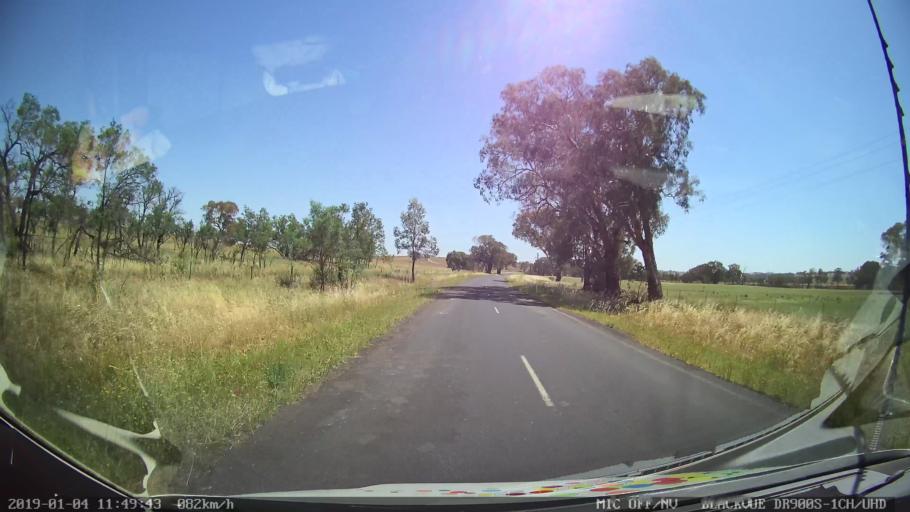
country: AU
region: New South Wales
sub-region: Cabonne
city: Molong
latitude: -32.9157
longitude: 148.7553
